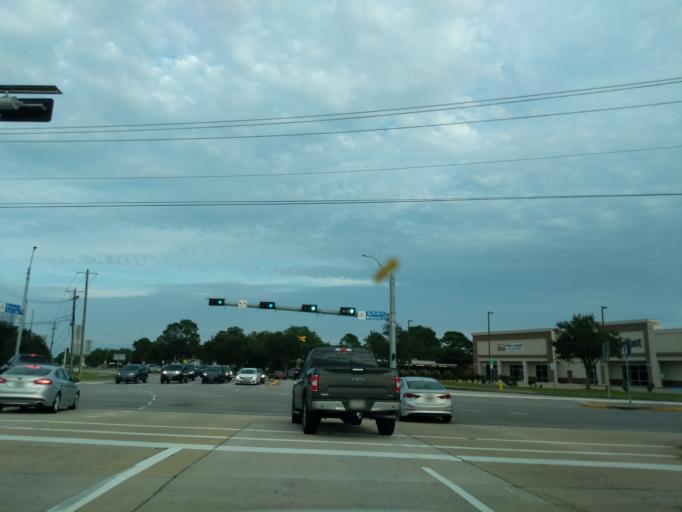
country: US
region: Texas
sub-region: Galveston County
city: League City
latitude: 29.5230
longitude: -95.0767
